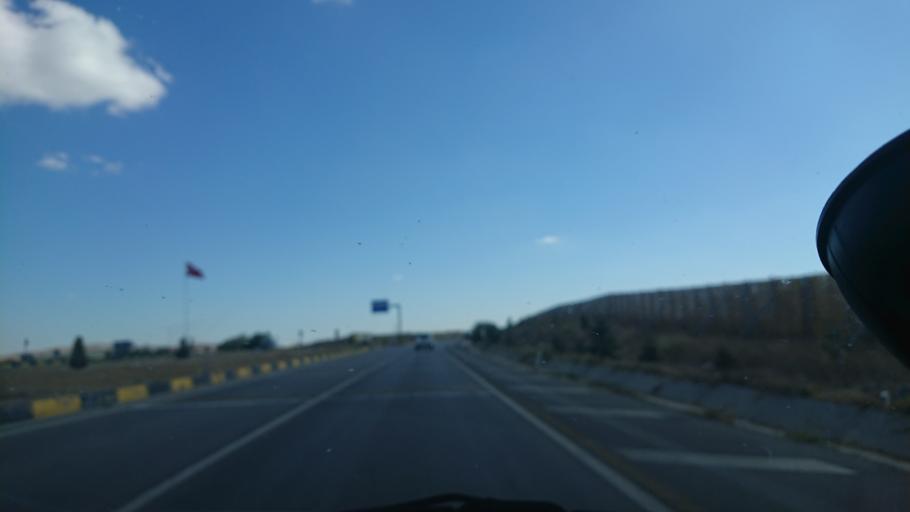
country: TR
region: Eskisehir
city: Mahmudiye
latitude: 39.5190
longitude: 30.9615
